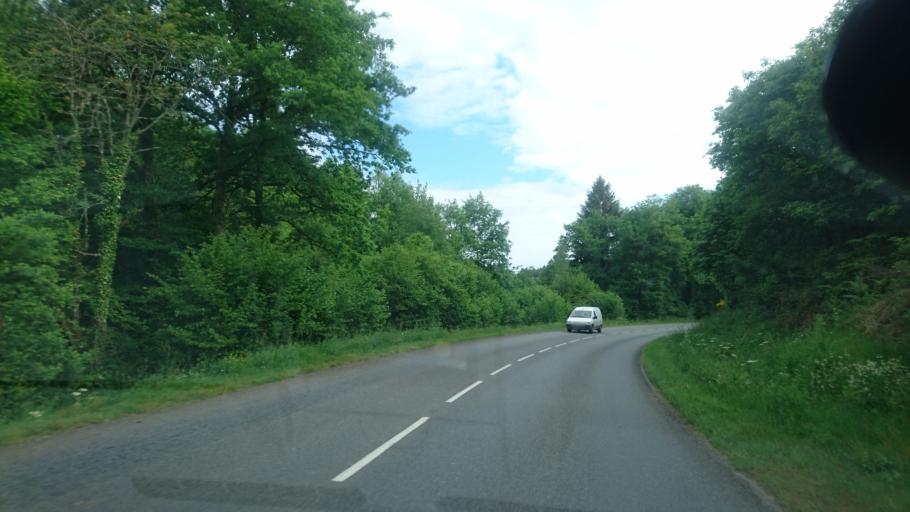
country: FR
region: Limousin
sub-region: Departement de la Haute-Vienne
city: Eymoutiers
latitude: 45.7748
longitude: 1.7595
